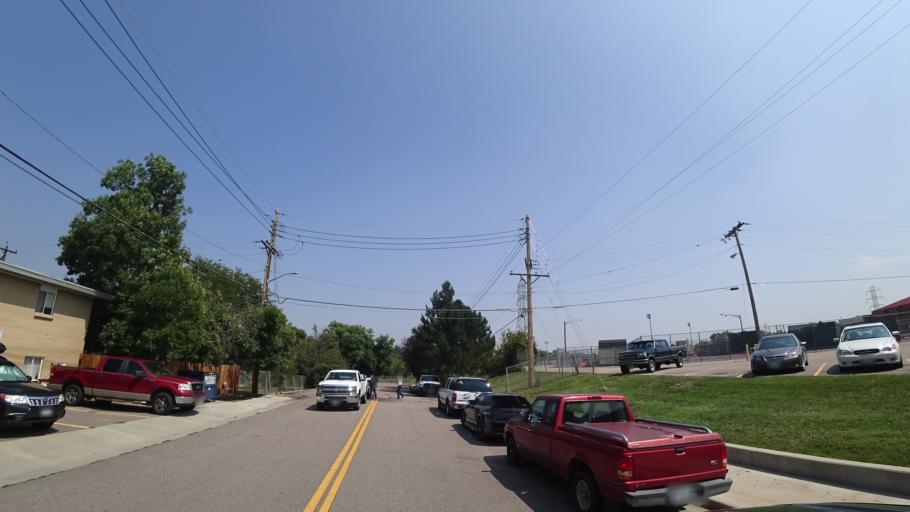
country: US
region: Colorado
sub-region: Arapahoe County
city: Littleton
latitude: 39.6150
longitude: -104.9843
